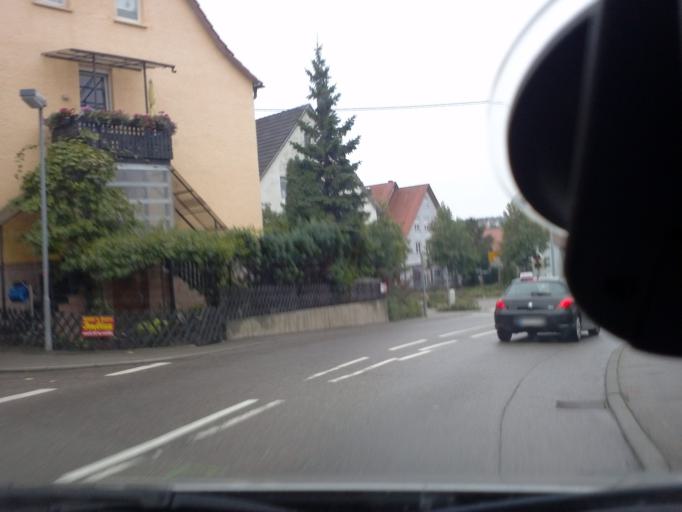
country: DE
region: Baden-Wuerttemberg
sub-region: Regierungsbezirk Stuttgart
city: Nordheim
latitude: 49.1096
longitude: 9.1264
